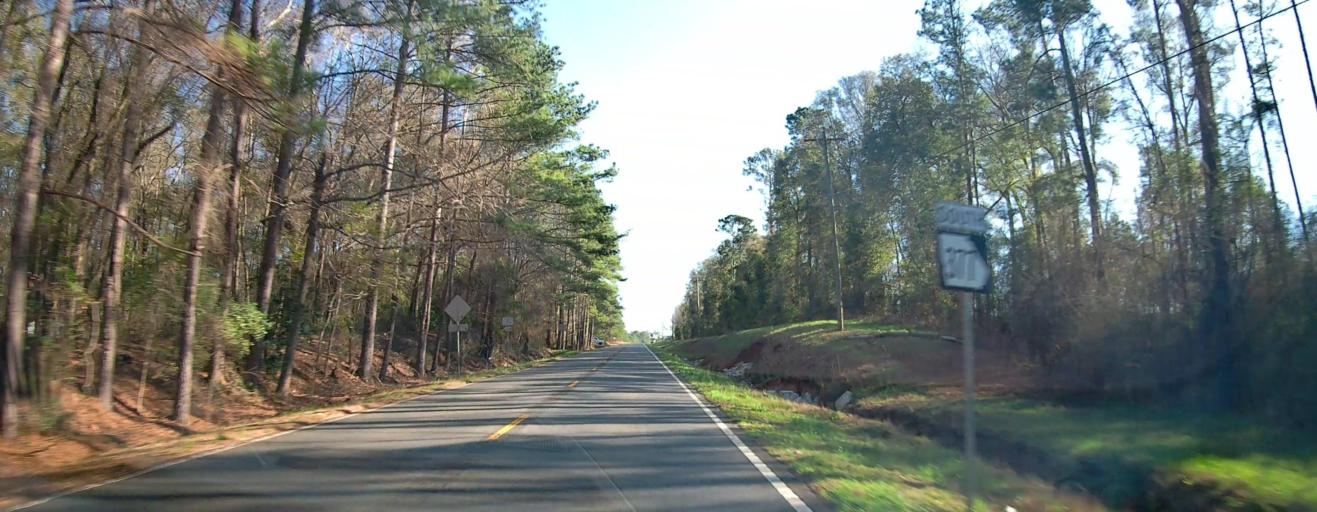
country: US
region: Georgia
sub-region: Sumter County
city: Americus
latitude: 32.0374
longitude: -84.2205
